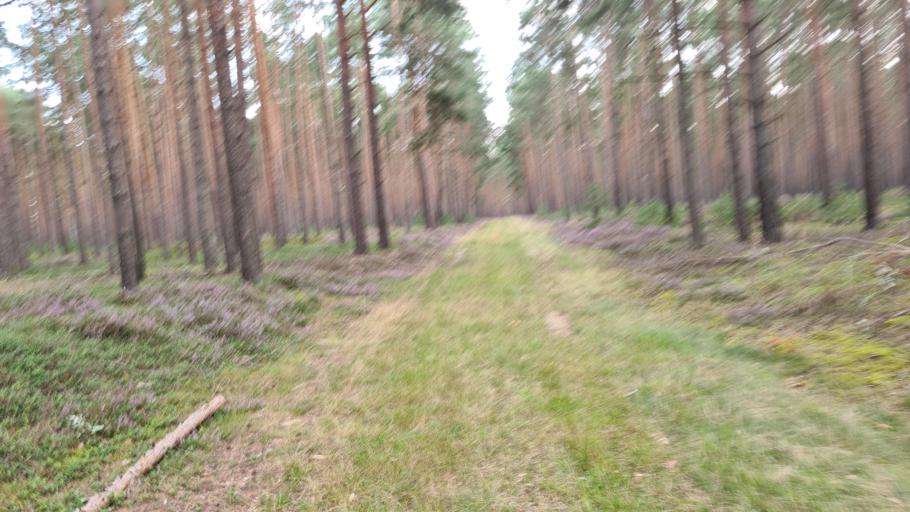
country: DE
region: Brandenburg
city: Schonborn
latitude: 51.6203
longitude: 13.4936
